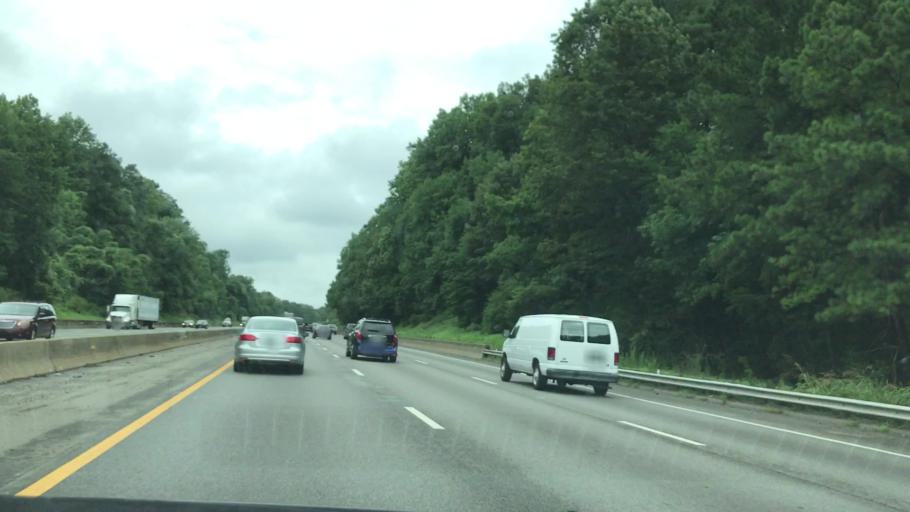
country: US
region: Virginia
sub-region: Chesterfield County
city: Chester
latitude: 37.3815
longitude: -77.4130
